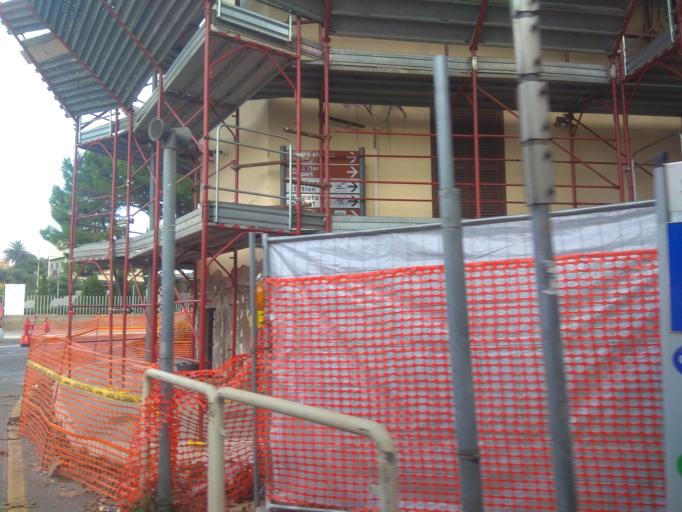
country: IT
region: Latium
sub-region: Citta metropolitana di Roma Capitale
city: Civitavecchia
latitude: 42.0967
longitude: 11.7896
